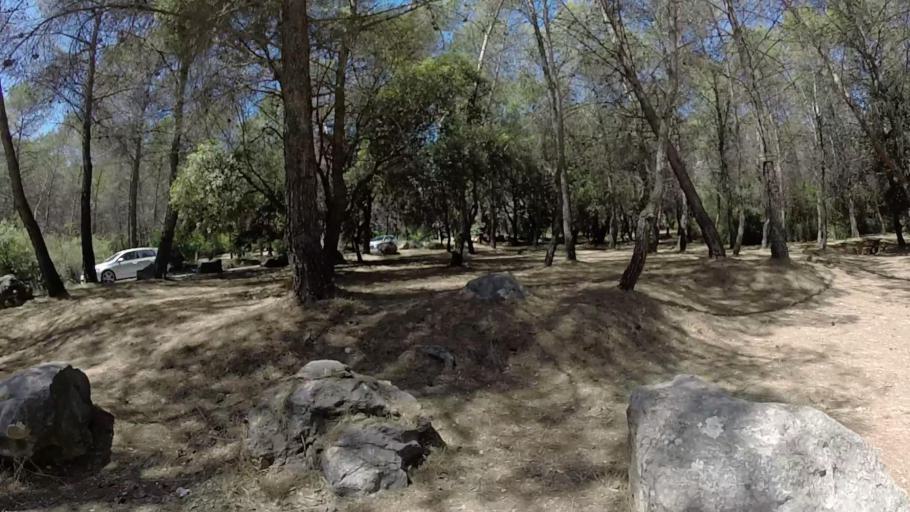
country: FR
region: Provence-Alpes-Cote d'Azur
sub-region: Departement des Alpes-Maritimes
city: Vallauris
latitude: 43.6046
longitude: 7.0495
